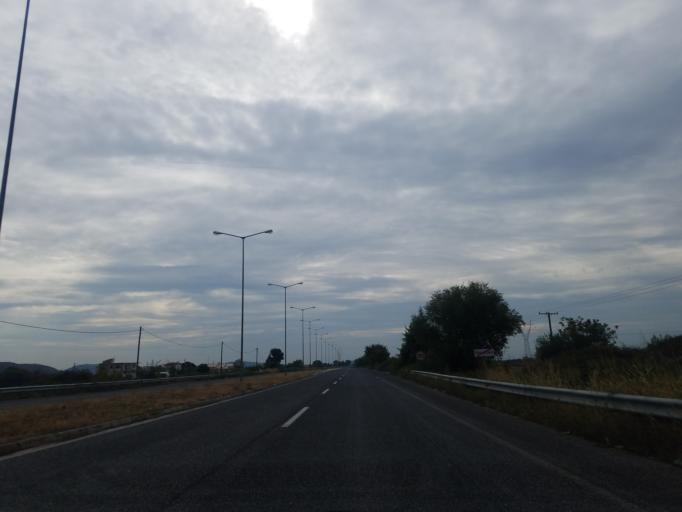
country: GR
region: Thessaly
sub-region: Trikala
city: Vasiliki
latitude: 39.6314
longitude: 21.7025
